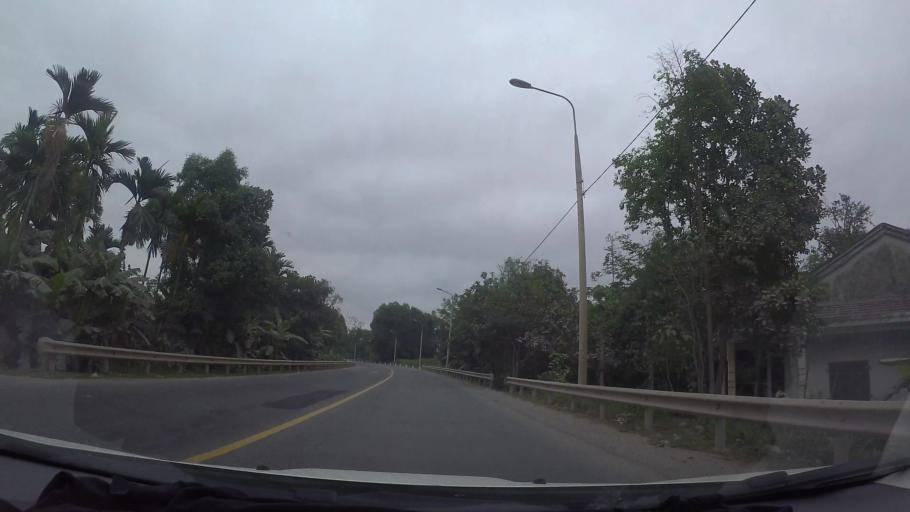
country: VN
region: Da Nang
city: Lien Chieu
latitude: 16.0802
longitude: 108.0849
